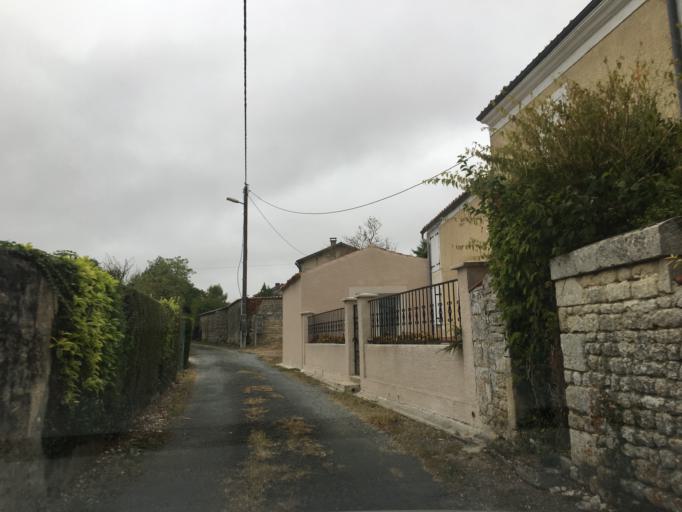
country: FR
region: Poitou-Charentes
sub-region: Departement des Deux-Sevres
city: Beauvoir-sur-Niort
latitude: 46.0792
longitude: -0.4922
